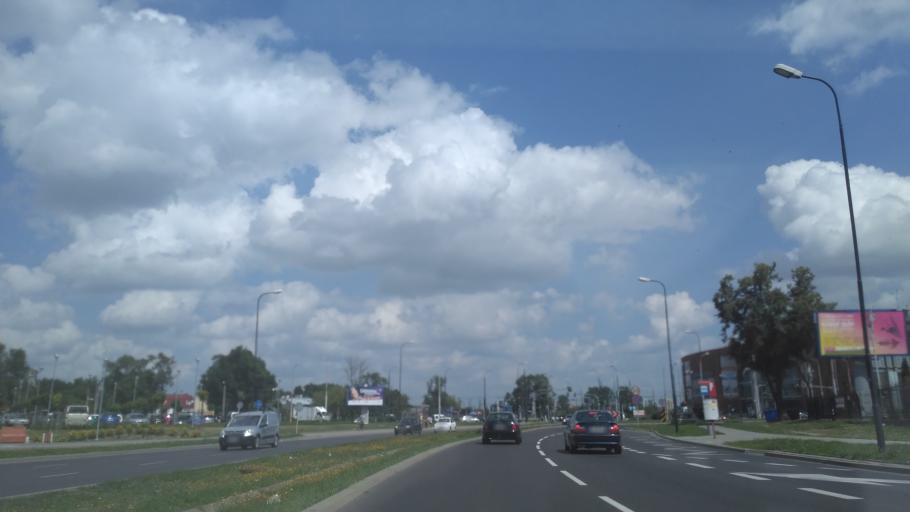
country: PL
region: Lublin Voivodeship
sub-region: Powiat lubelski
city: Lublin
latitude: 51.2366
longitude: 22.5698
